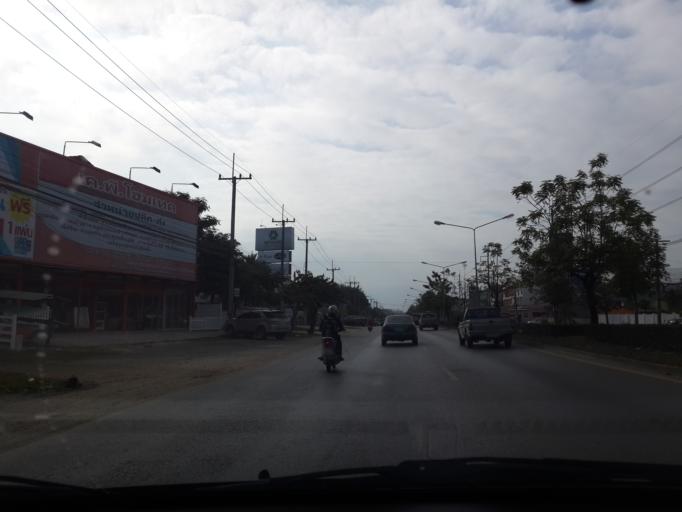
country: TH
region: Chiang Mai
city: San Sai
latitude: 18.8834
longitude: 99.0140
